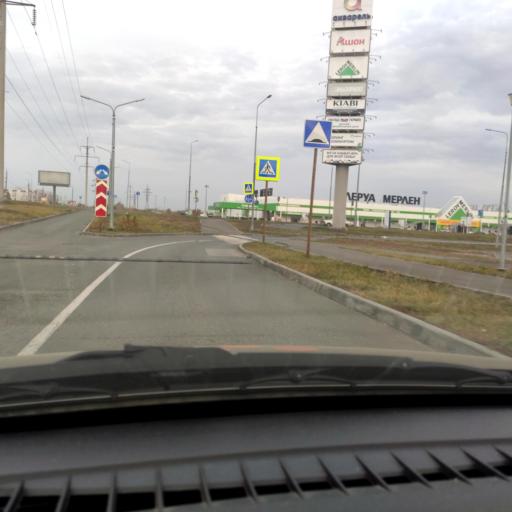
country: RU
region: Samara
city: Tol'yatti
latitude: 53.5489
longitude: 49.3428
